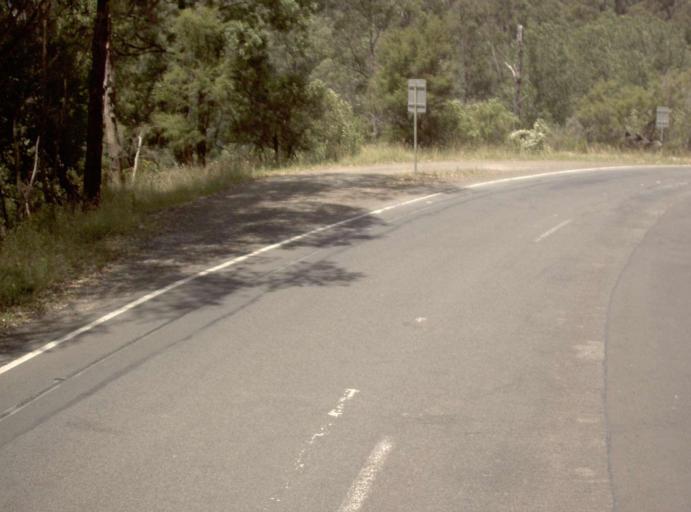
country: AU
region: Victoria
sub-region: Latrobe
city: Traralgon
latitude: -37.9562
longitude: 146.4231
